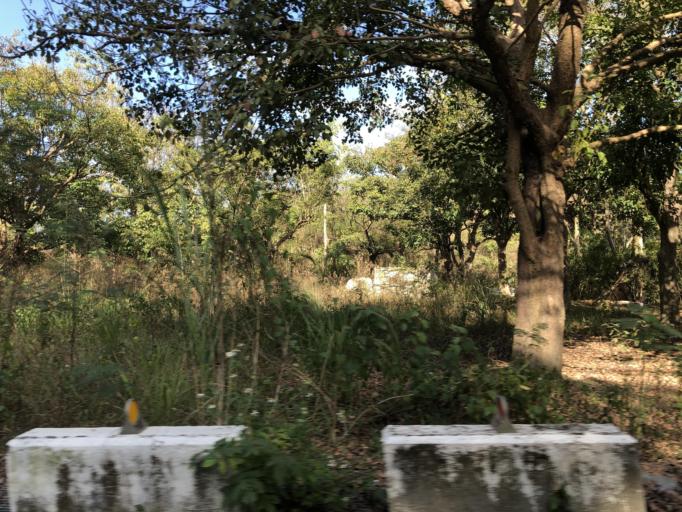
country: TW
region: Taiwan
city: Yujing
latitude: 23.0170
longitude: 120.3979
